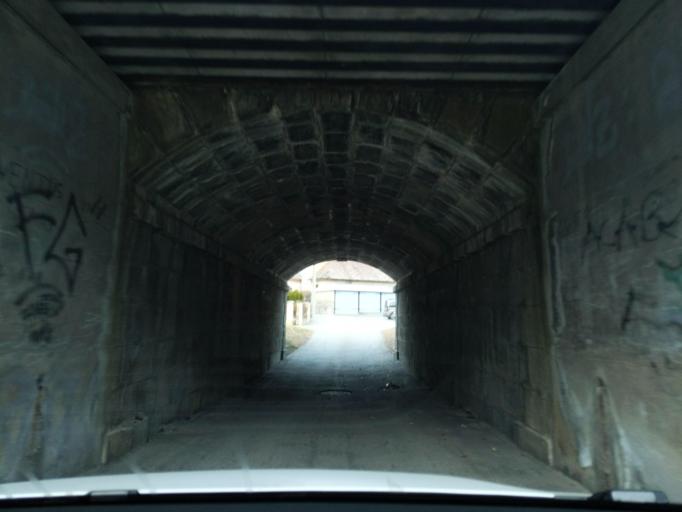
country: FR
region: Rhone-Alpes
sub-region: Departement de la Savoie
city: Saint-Michel-de-Maurienne
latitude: 45.2184
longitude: 6.4675
